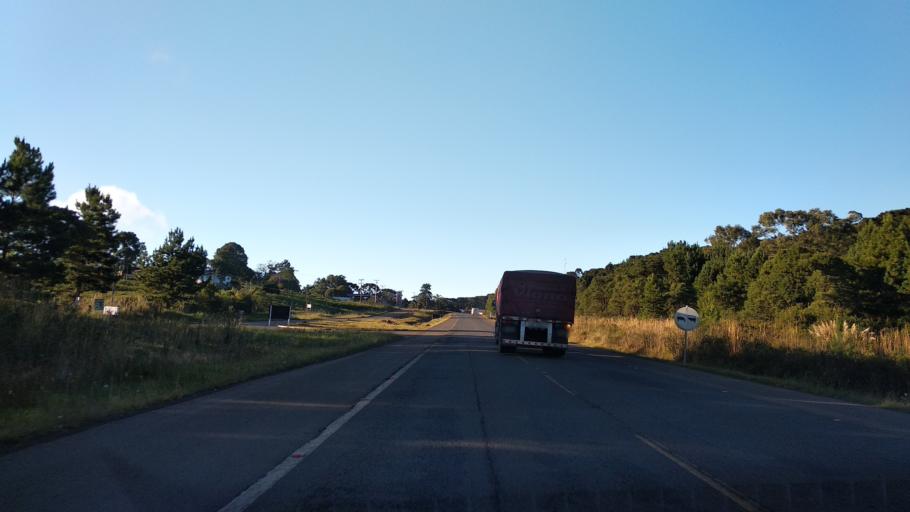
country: BR
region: Santa Catarina
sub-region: Correia Pinto
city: Correia Pinto
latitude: -27.6429
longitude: -50.5952
